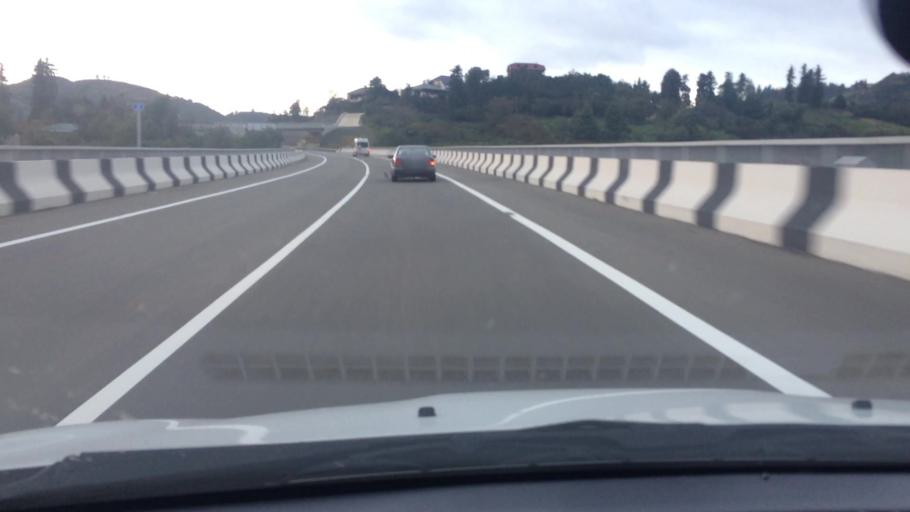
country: GE
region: Ajaria
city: Makhinjauri
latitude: 41.7160
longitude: 41.7519
